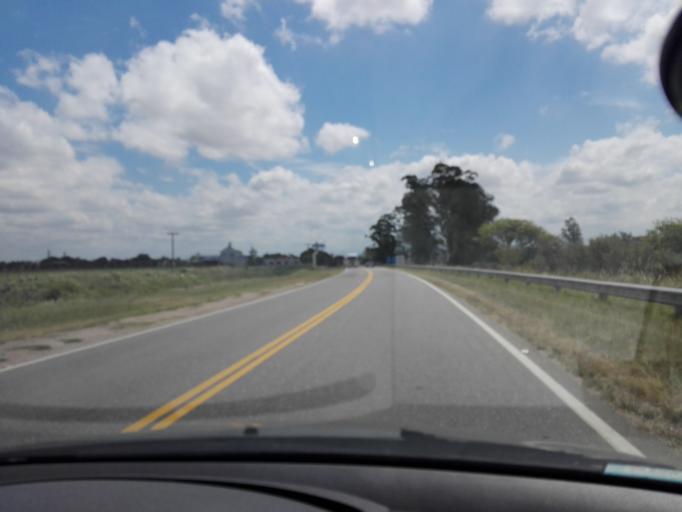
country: AR
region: Cordoba
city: Toledo
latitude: -31.6476
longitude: -64.0814
